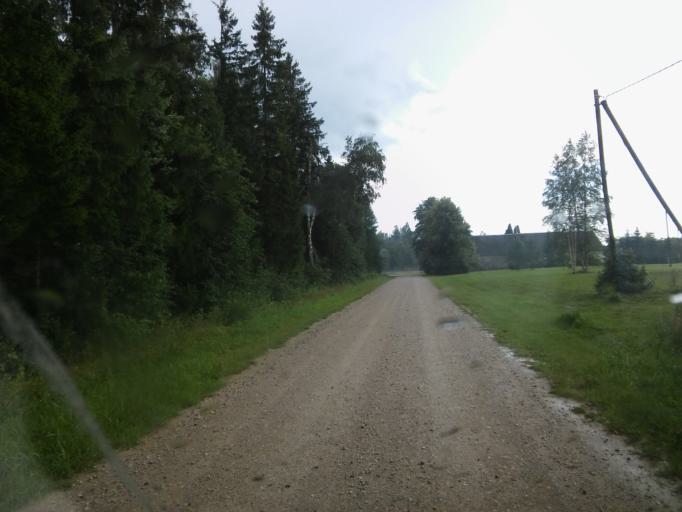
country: EE
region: Paernumaa
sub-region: Halinga vald
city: Parnu-Jaagupi
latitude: 58.7876
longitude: 24.5996
